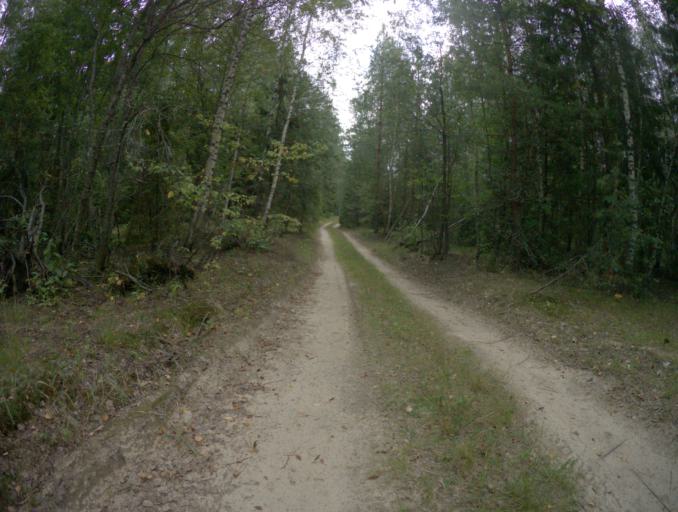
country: RU
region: Vladimir
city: Vorsha
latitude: 55.9652
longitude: 40.1622
